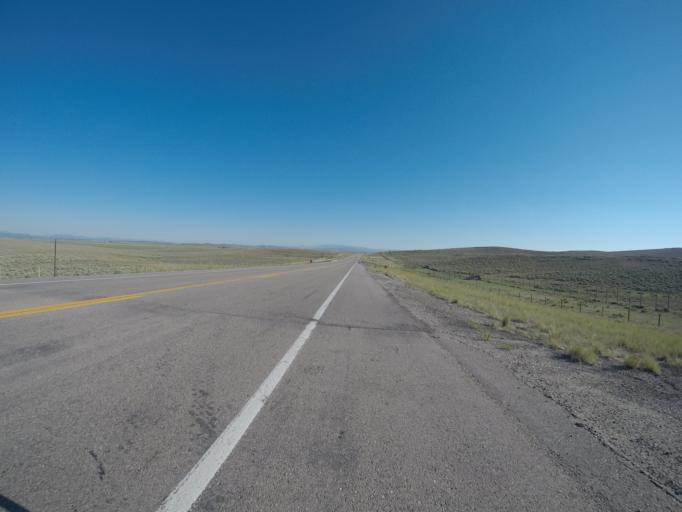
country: US
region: Wyoming
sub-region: Sublette County
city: Pinedale
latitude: 42.9167
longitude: -110.0792
